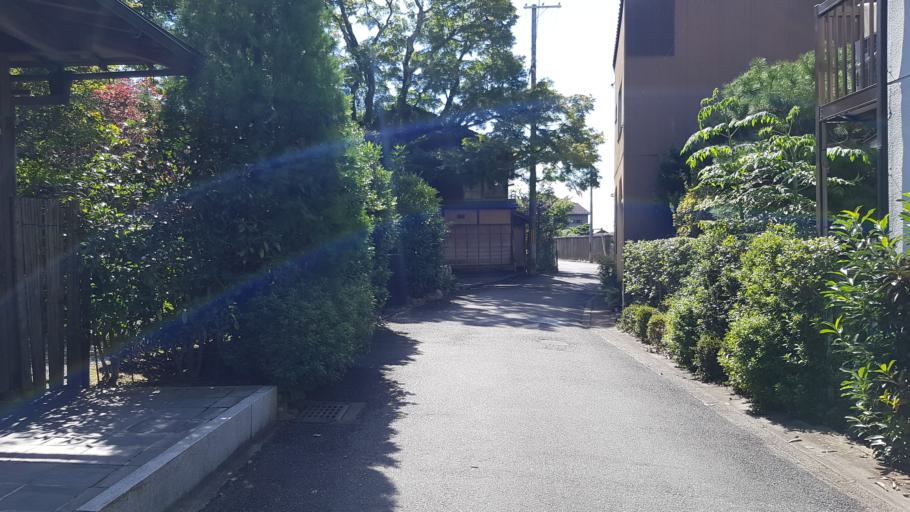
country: JP
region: Kyoto
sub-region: Kyoto-shi
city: Kamigyo-ku
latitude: 35.0216
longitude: 135.7963
